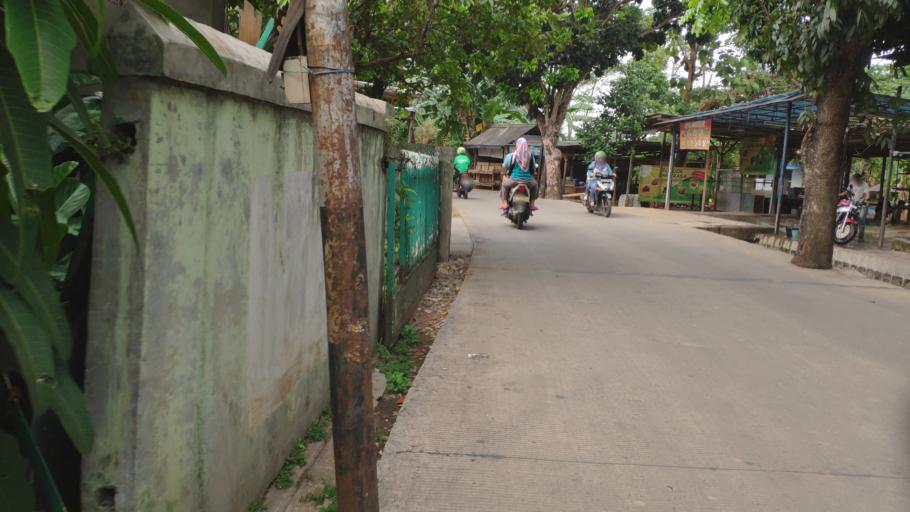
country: ID
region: West Java
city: Depok
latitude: -6.3394
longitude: 106.8134
